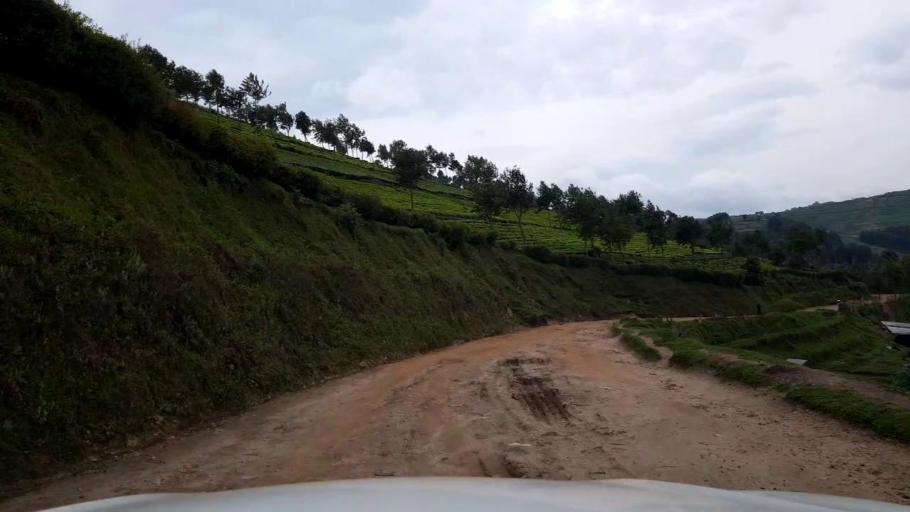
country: RW
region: Western Province
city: Kibuye
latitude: -1.9562
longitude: 29.4232
